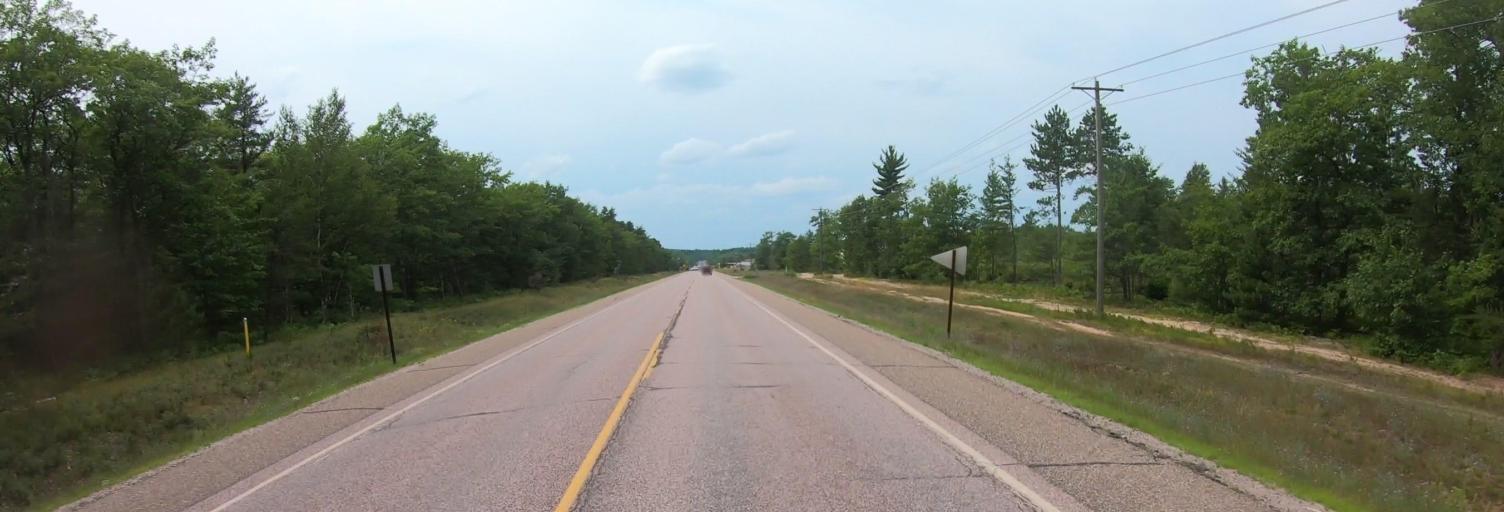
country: US
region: Michigan
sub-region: Marquette County
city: Harvey
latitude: 46.4613
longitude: -87.4180
